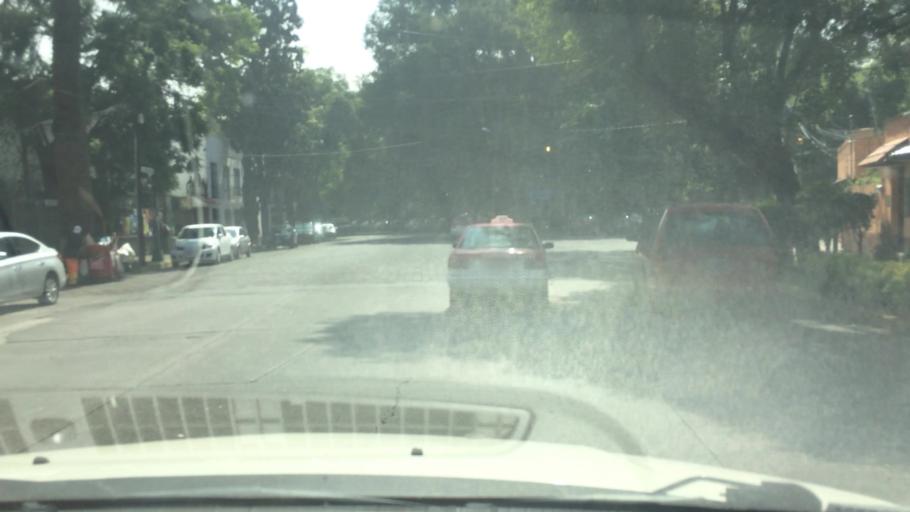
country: MX
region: Mexico City
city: Coyoacan
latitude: 19.3551
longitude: -99.1505
